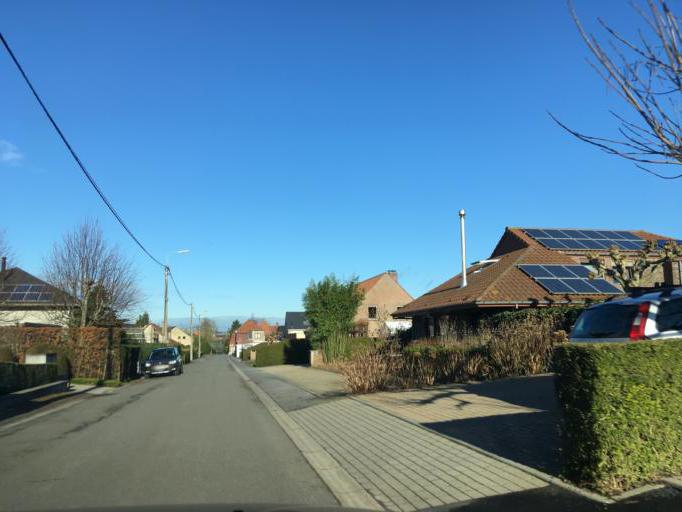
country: BE
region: Flanders
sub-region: Provincie West-Vlaanderen
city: Roeselare
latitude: 50.9204
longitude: 3.1223
